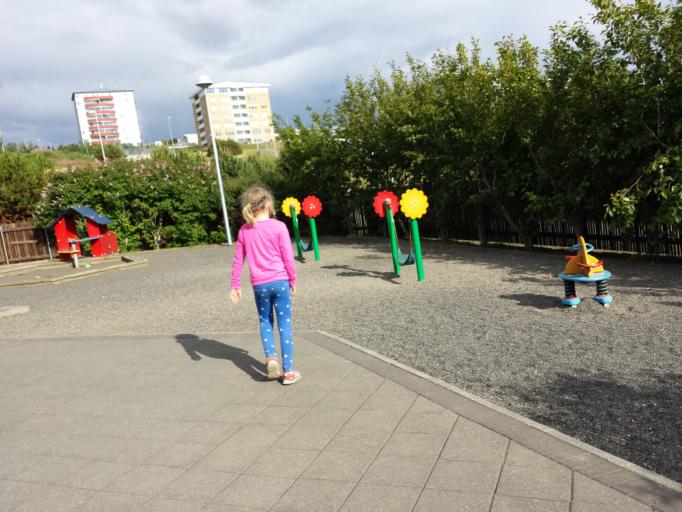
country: IS
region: Capital Region
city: Reykjavik
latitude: 64.0940
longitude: -21.8569
